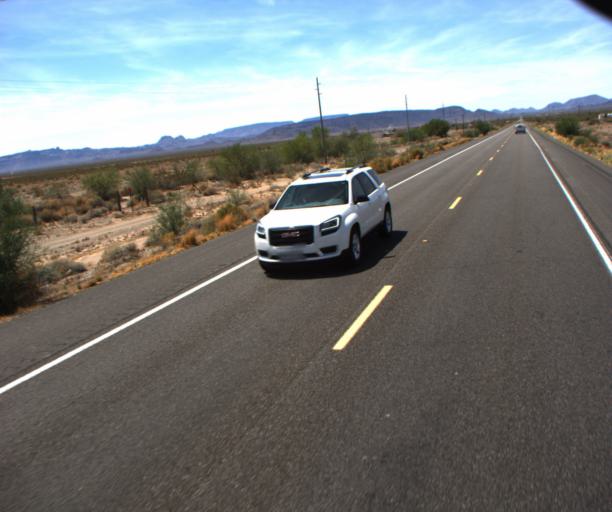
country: US
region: Arizona
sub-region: La Paz County
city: Salome
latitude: 33.7114
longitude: -113.8052
